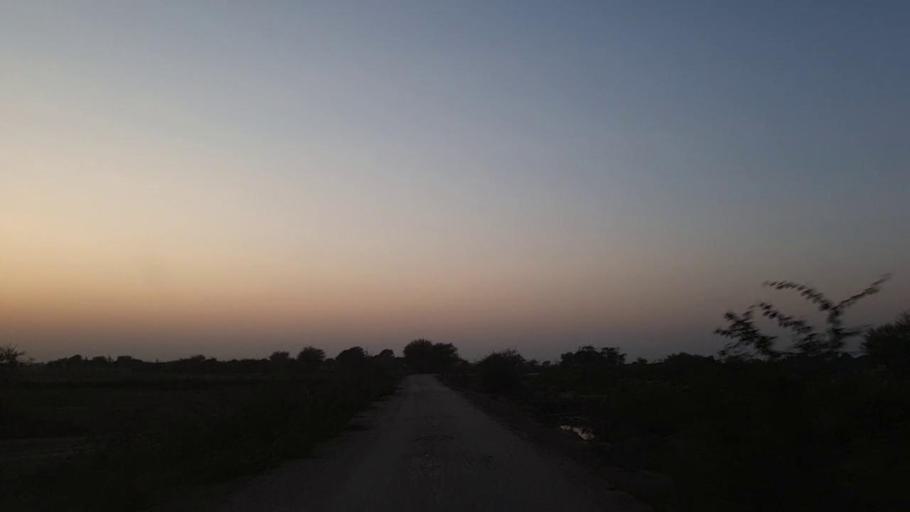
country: PK
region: Sindh
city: Naukot
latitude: 24.8847
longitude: 69.3875
